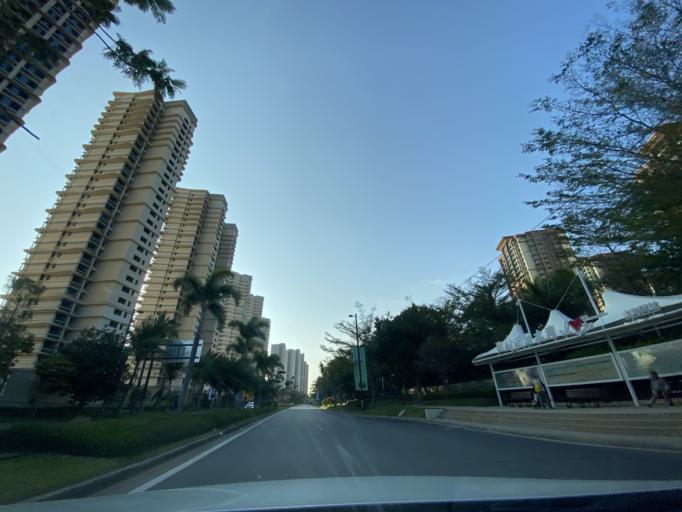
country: CN
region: Hainan
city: Xincun
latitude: 18.4221
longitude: 109.9420
